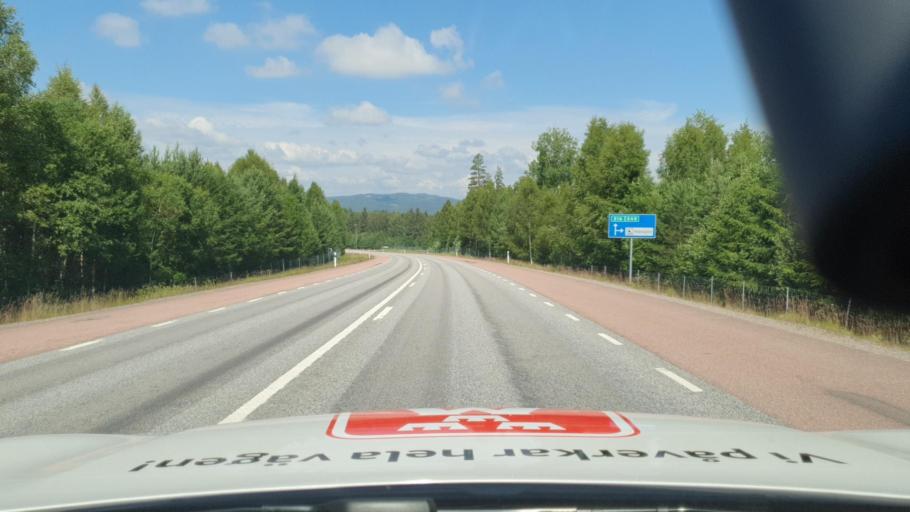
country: SE
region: Vaermland
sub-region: Torsby Kommun
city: Torsby
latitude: 60.1979
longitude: 13.0219
